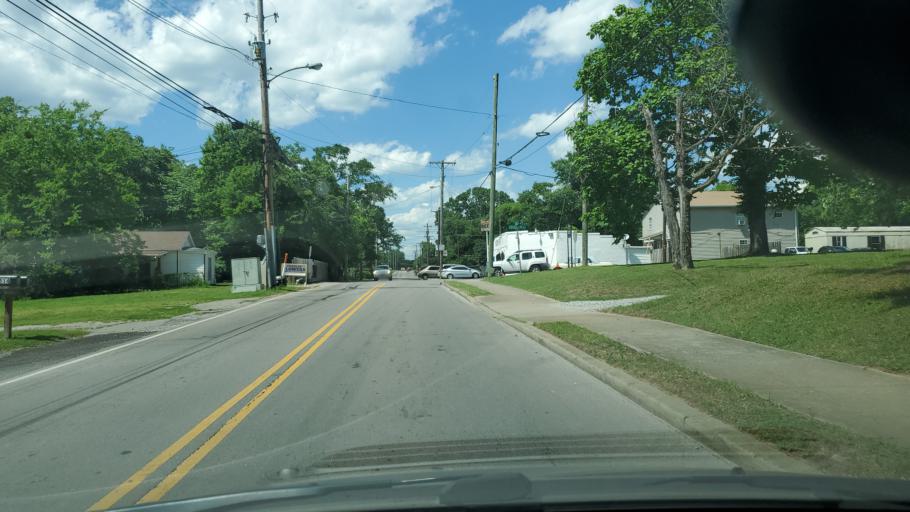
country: US
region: Tennessee
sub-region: Davidson County
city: Nashville
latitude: 36.2006
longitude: -86.7584
